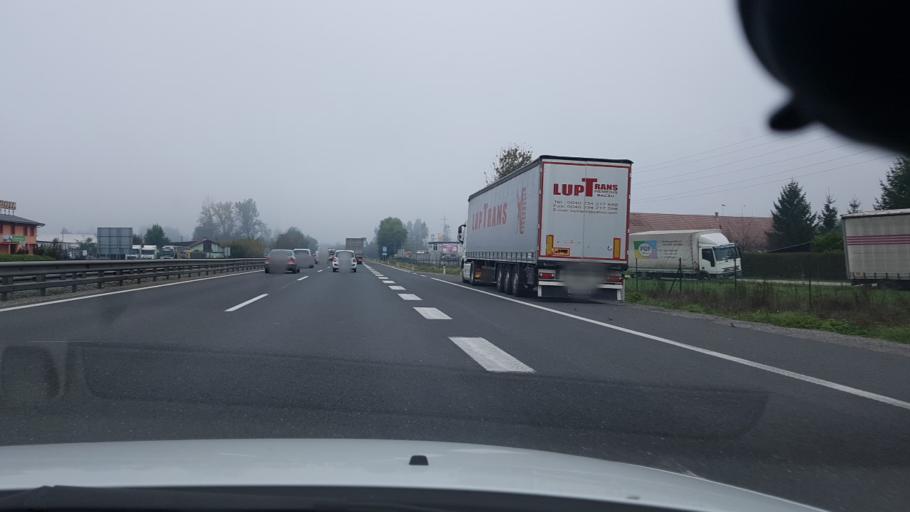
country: SI
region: Ljubljana
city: Ljubljana
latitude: 46.0314
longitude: 14.4739
